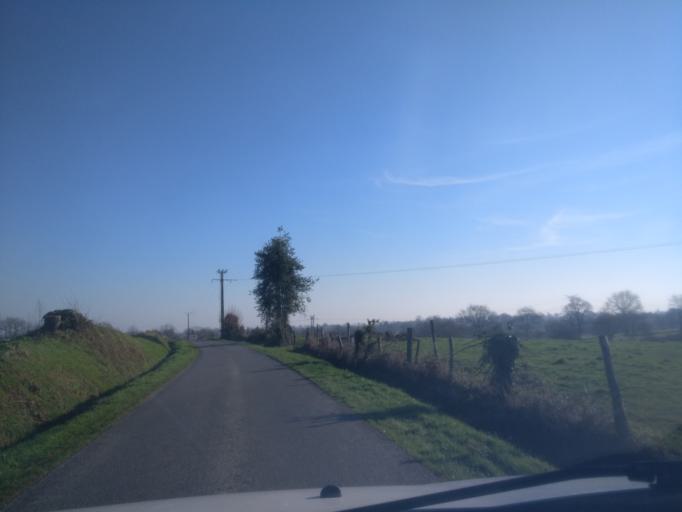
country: FR
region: Brittany
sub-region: Departement d'Ille-et-Vilaine
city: Livre-sur-Changeon
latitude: 48.2426
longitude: -1.3525
